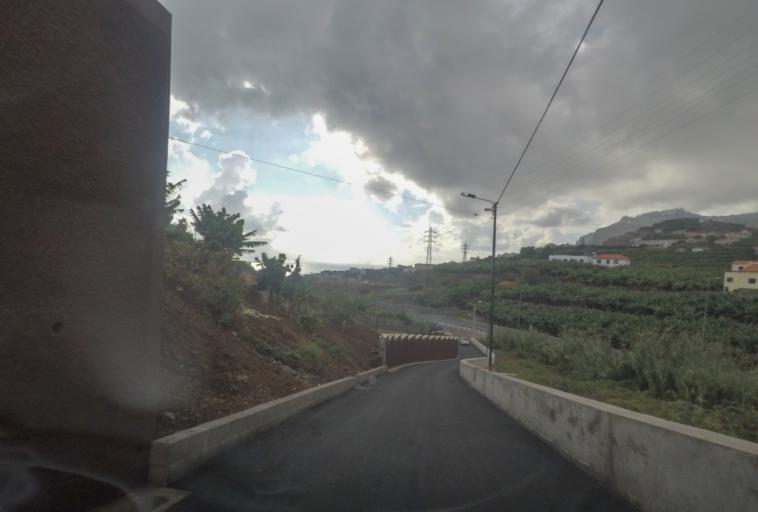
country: PT
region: Madeira
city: Camara de Lobos
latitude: 32.6493
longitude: -16.9630
